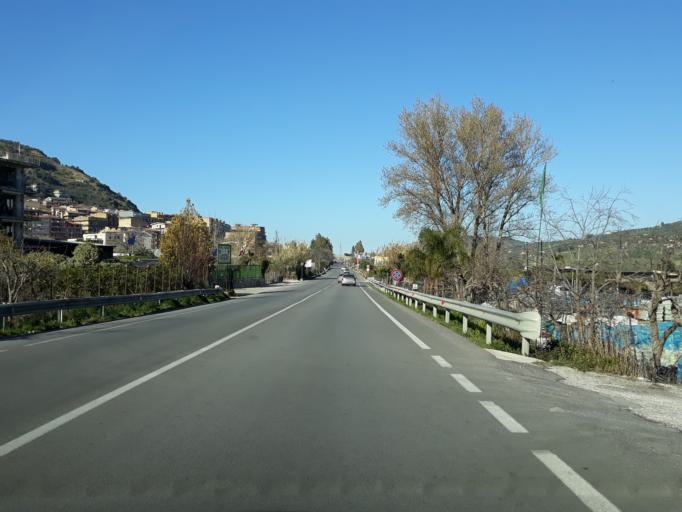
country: IT
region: Sicily
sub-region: Palermo
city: Misilmeri
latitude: 38.0304
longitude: 13.4565
